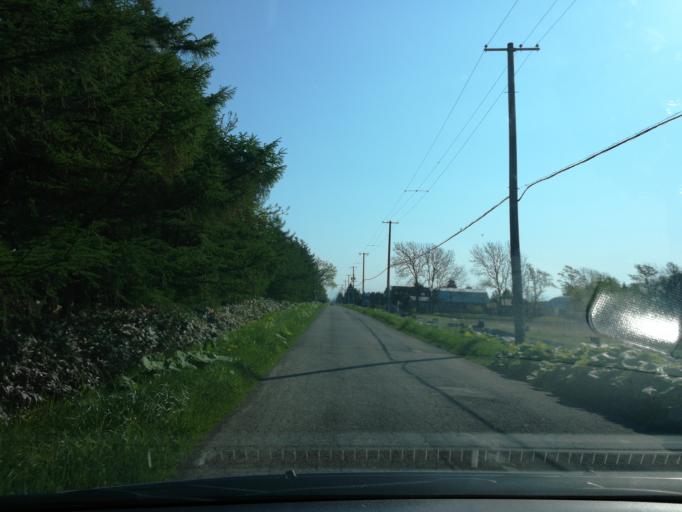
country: JP
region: Hokkaido
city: Ebetsu
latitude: 43.1201
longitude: 141.6550
